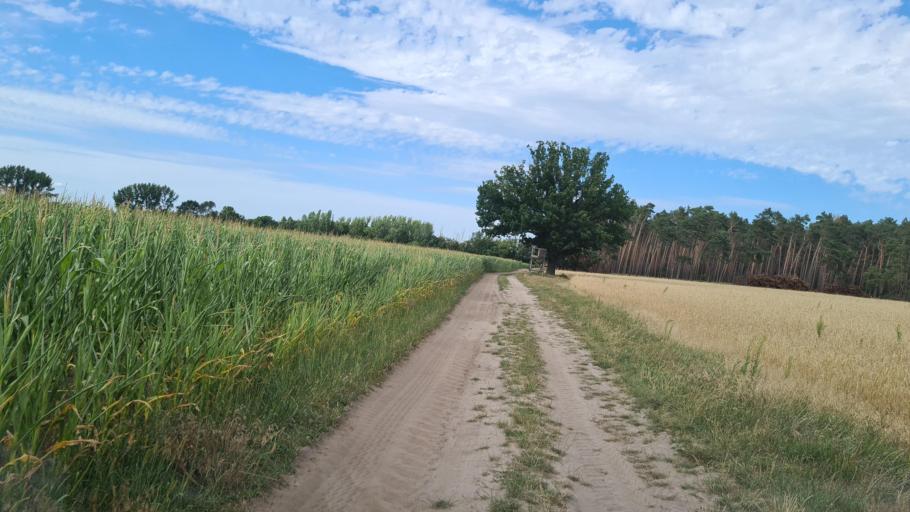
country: DE
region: Saxony-Anhalt
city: Holzdorf
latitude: 51.8220
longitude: 13.1967
